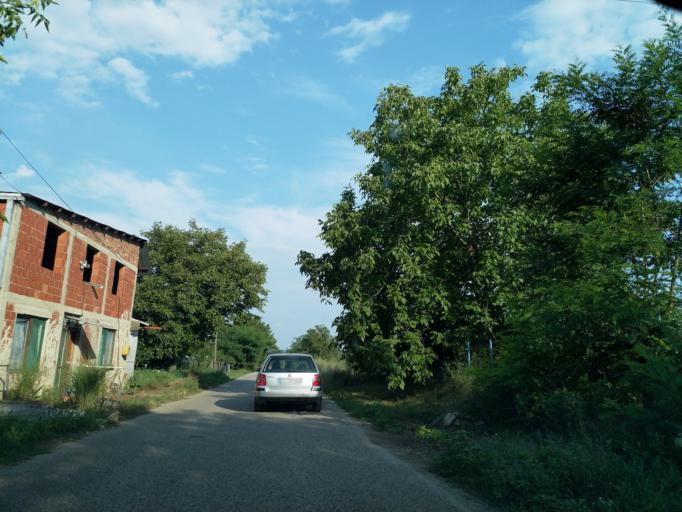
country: RS
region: Central Serbia
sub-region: Pomoravski Okrug
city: Jagodina
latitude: 43.9806
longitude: 21.2270
